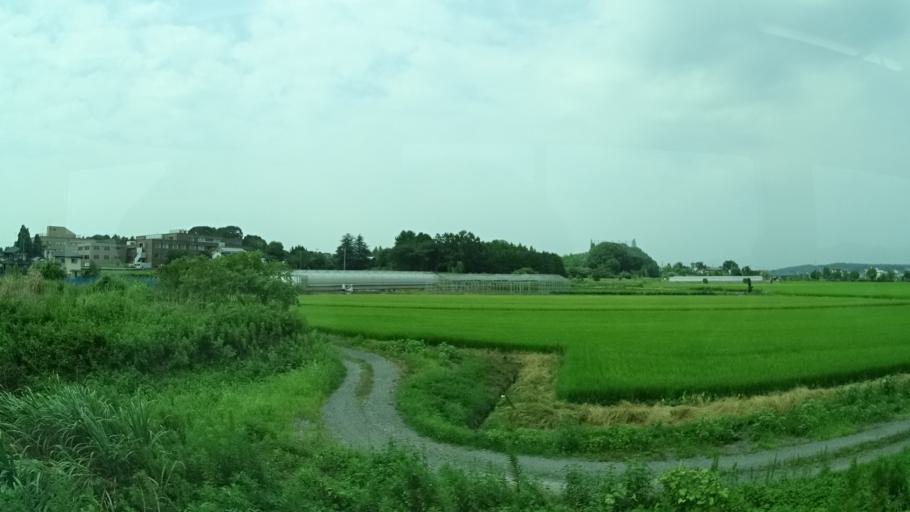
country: JP
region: Tochigi
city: Mashiko
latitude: 36.4573
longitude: 140.0809
